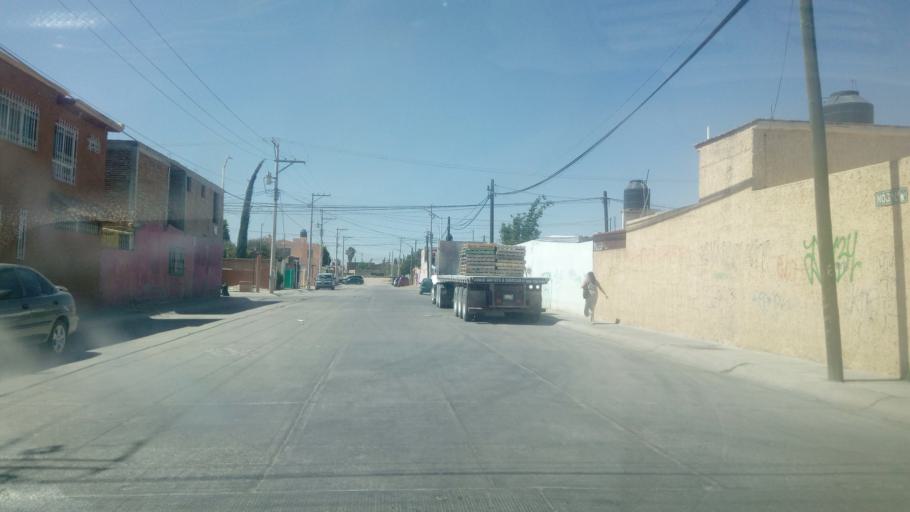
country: MX
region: Durango
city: Victoria de Durango
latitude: 24.0046
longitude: -104.6285
